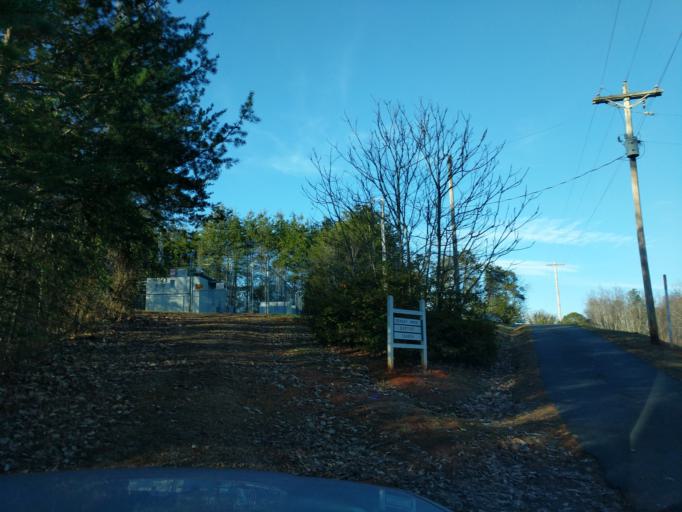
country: US
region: North Carolina
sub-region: Rutherford County
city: Lake Lure
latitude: 35.4079
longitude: -82.1722
